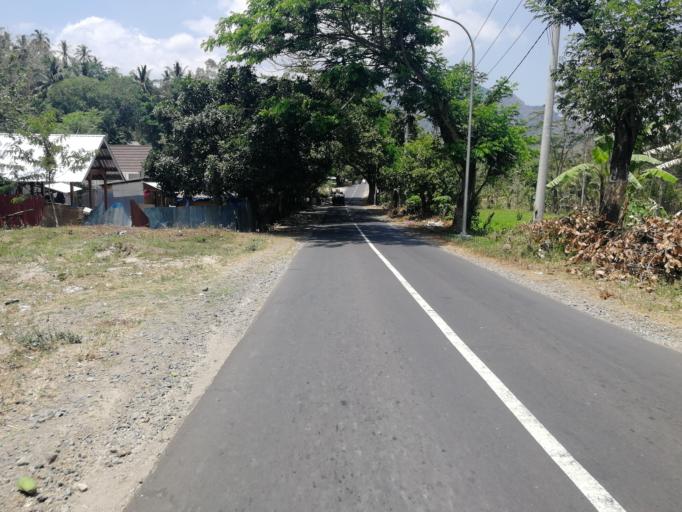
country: ID
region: West Nusa Tenggara
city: Karangsubagan
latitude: -8.4359
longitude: 116.0873
